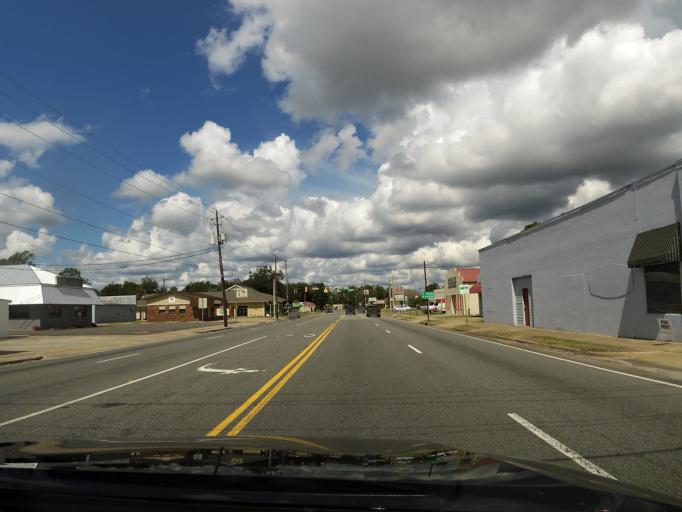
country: US
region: Georgia
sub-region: Charlton County
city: Folkston
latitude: 30.8317
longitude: -82.0060
